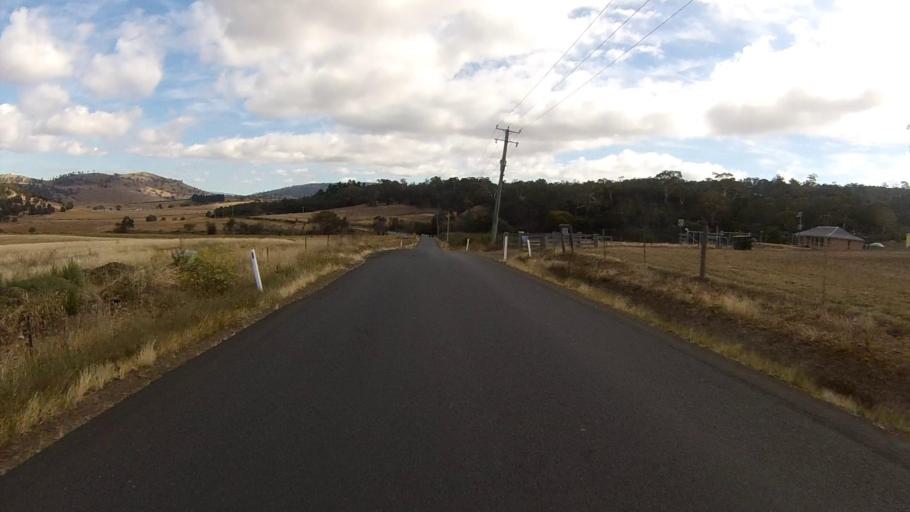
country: AU
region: Tasmania
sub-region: Brighton
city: Old Beach
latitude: -42.7555
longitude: 147.3050
